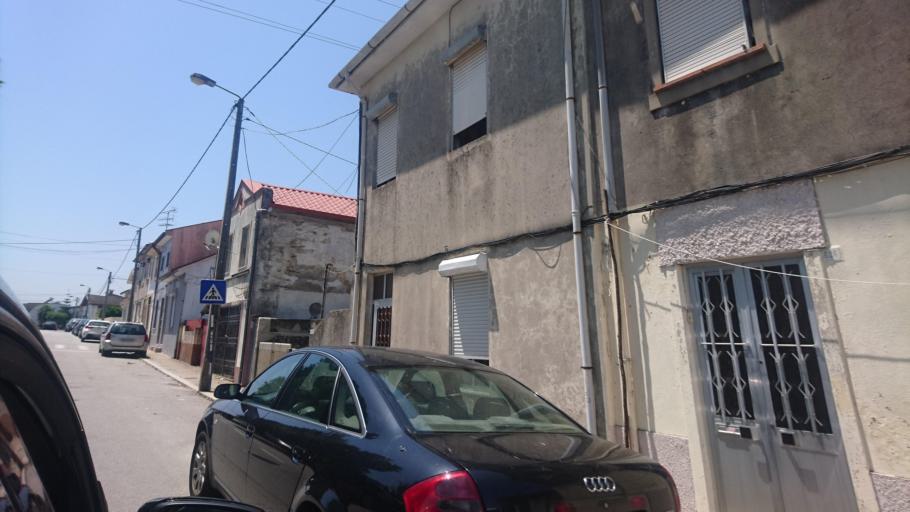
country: PT
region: Porto
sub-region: Gondomar
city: Rio Tinto
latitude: 41.1588
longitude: -8.5564
